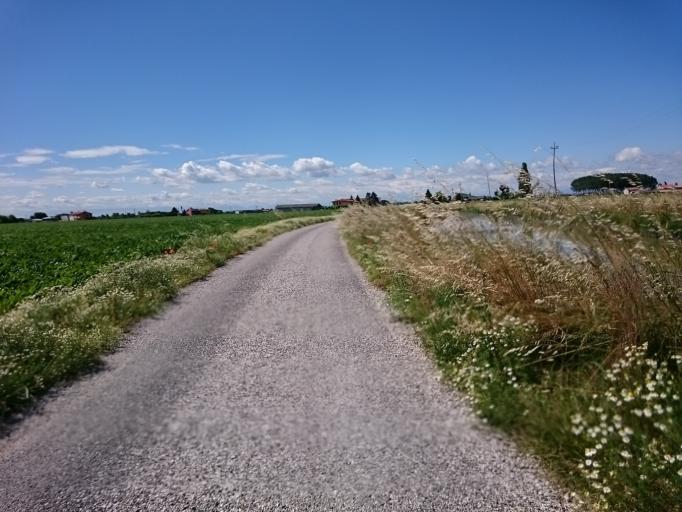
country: IT
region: Veneto
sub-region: Provincia di Padova
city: Codevigo
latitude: 45.2568
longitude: 12.0978
